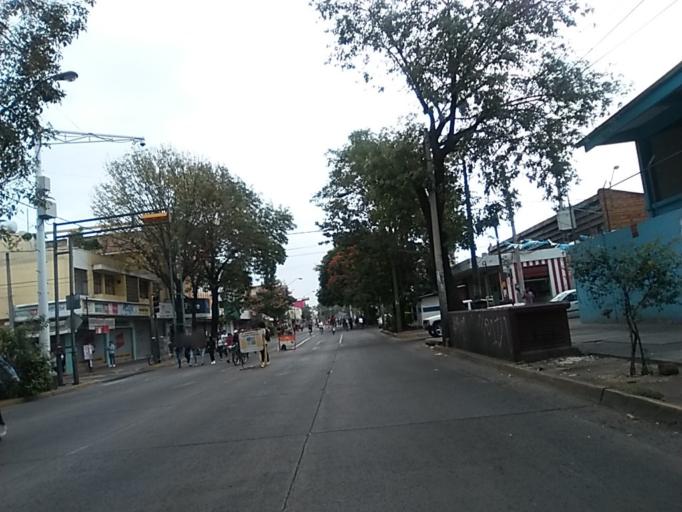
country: MX
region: Jalisco
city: Tlaquepaque
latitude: 20.6733
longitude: -103.3336
